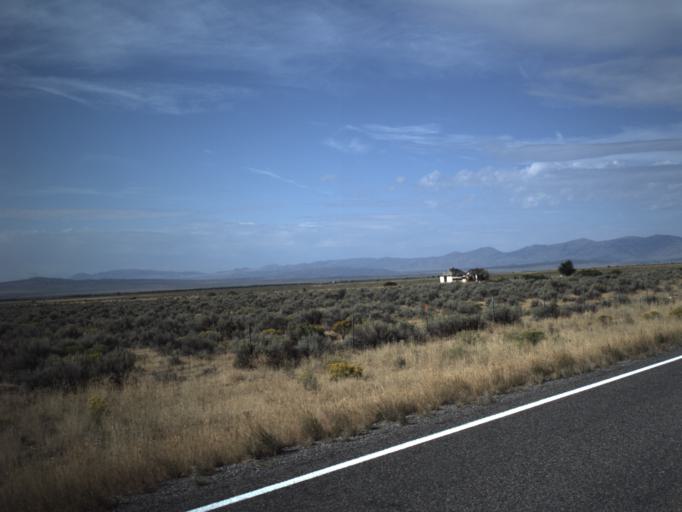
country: US
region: Idaho
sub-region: Cassia County
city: Burley
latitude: 41.8168
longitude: -113.3463
